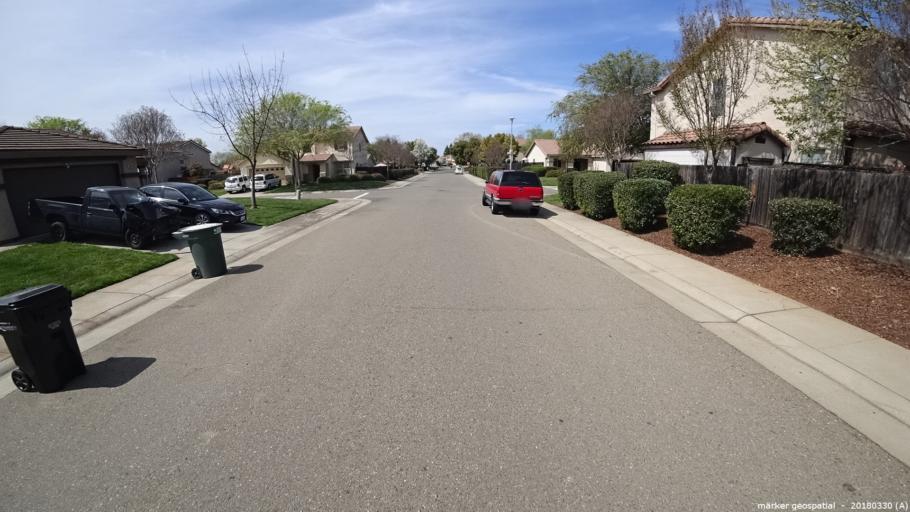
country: US
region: California
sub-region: Sacramento County
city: Rancho Cordova
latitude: 38.5446
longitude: -121.2821
